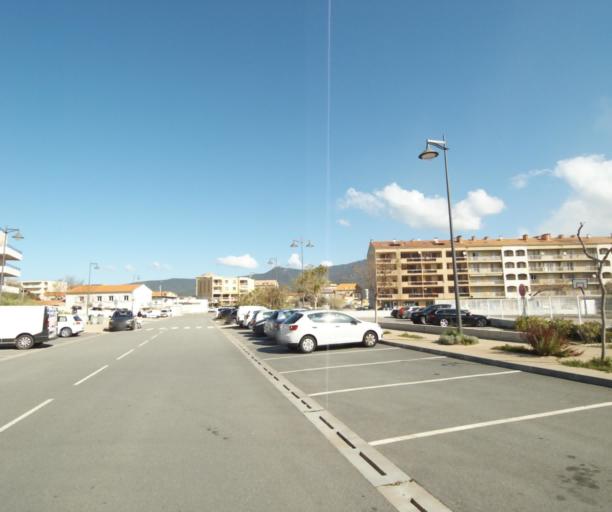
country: FR
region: Corsica
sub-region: Departement de la Corse-du-Sud
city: Propriano
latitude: 41.6735
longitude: 8.8996
